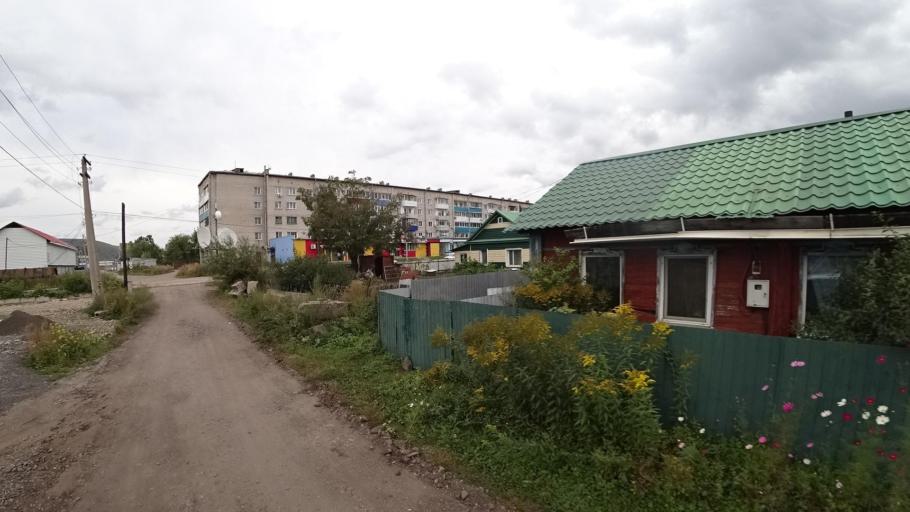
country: RU
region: Jewish Autonomous Oblast
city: Khingansk
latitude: 49.0080
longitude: 131.0509
